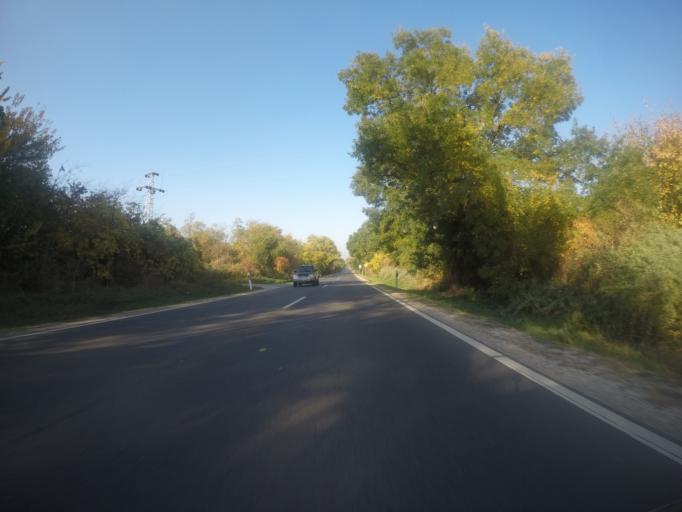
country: HU
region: Pest
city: Szazhalombatta
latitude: 47.3131
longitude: 18.8892
